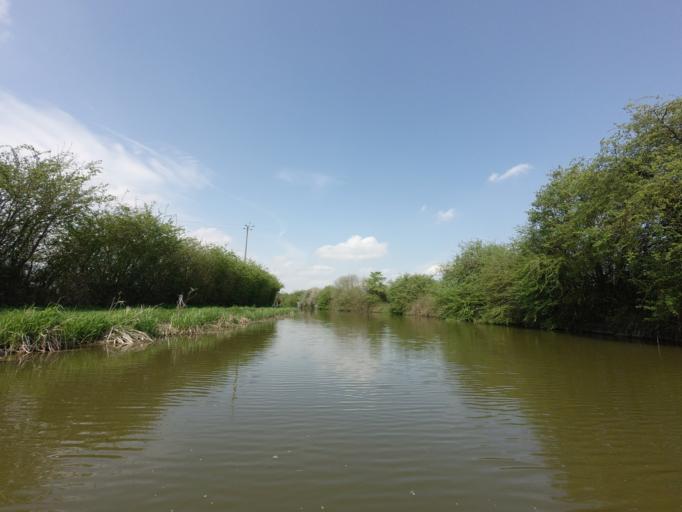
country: GB
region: England
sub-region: Buckinghamshire
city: Cheddington
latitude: 51.8756
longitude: -0.6556
